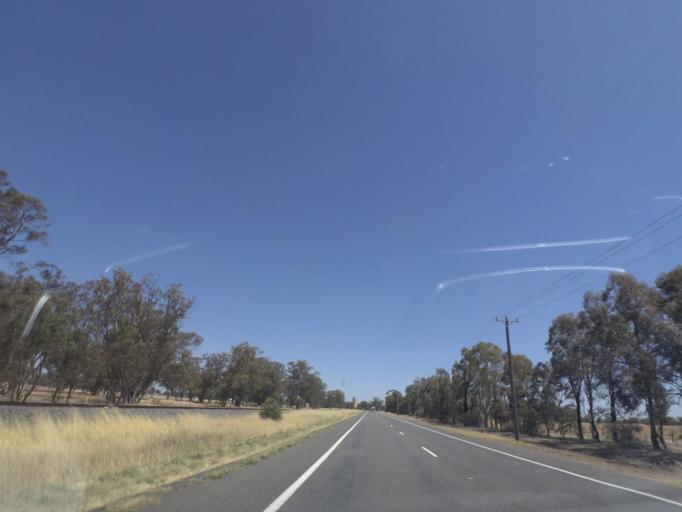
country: AU
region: Victoria
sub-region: Greater Shepparton
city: Shepparton
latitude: -36.2297
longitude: 145.4318
